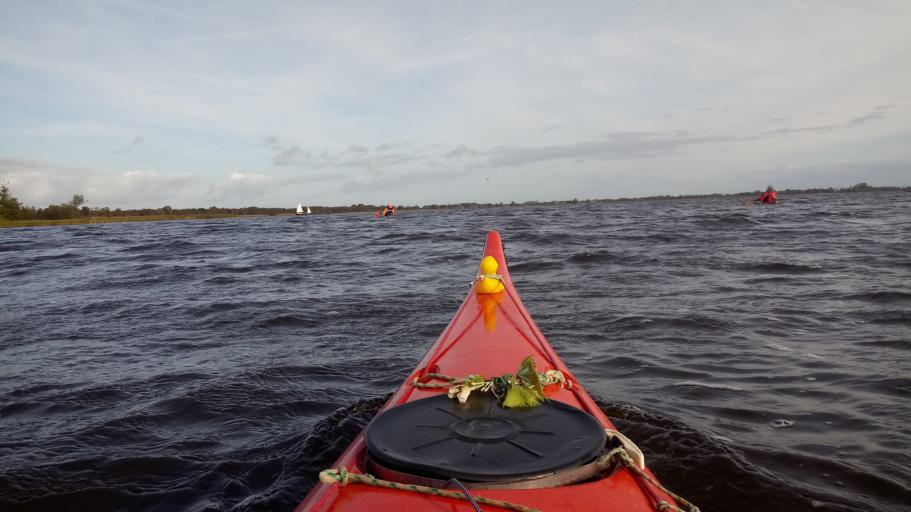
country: NL
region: Overijssel
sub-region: Gemeente Steenwijkerland
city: Sint Jansklooster
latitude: 52.7030
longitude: 6.0322
